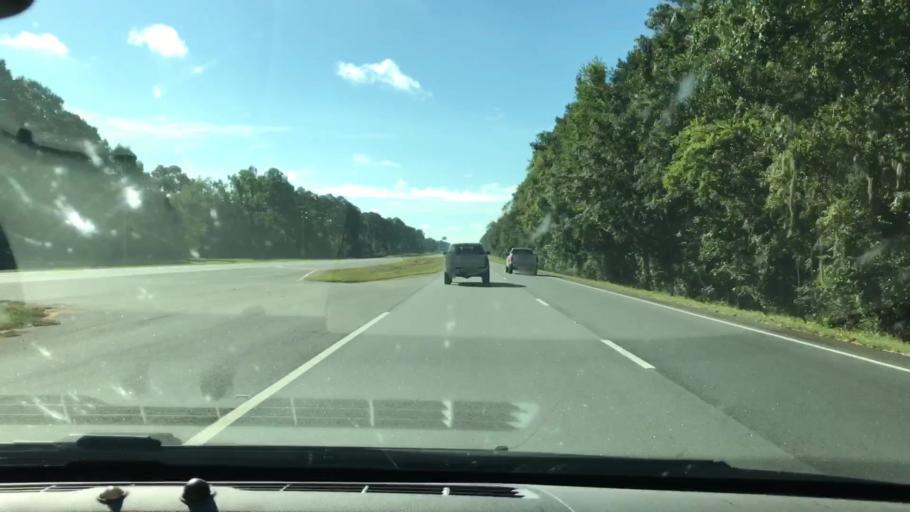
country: US
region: Georgia
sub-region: Lee County
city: Leesburg
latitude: 31.6555
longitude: -84.2701
